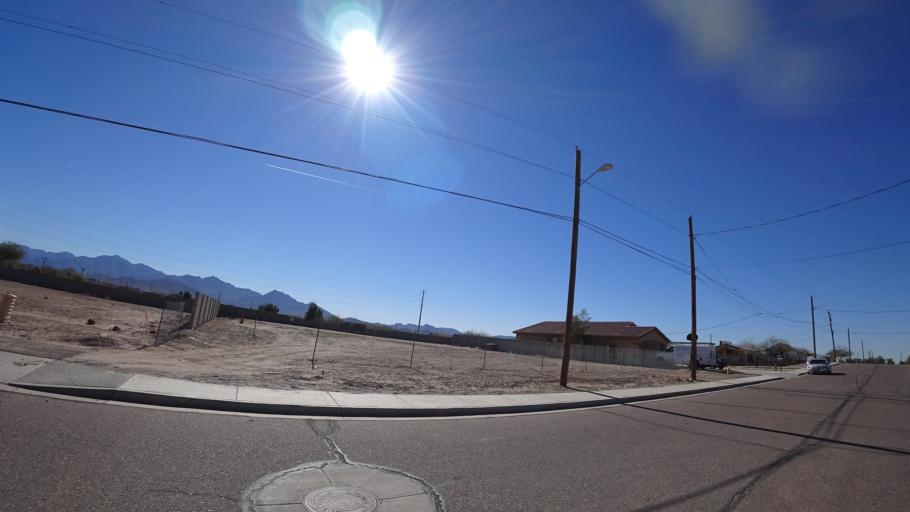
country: US
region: Arizona
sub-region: Maricopa County
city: Avondale
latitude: 33.4134
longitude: -112.3327
